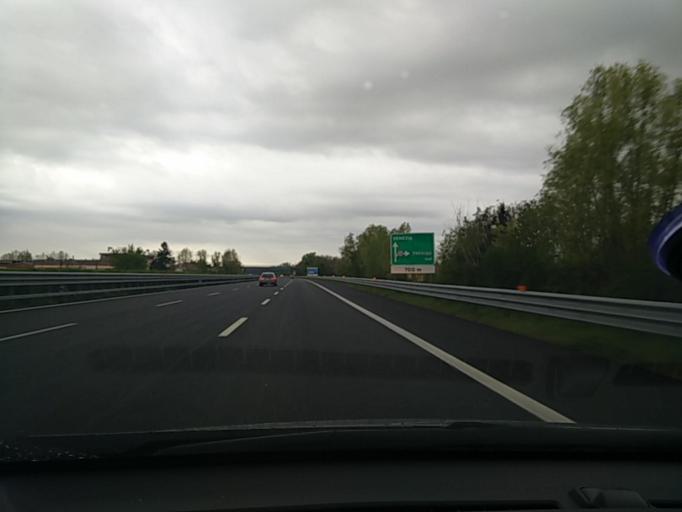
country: IT
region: Veneto
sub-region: Provincia di Treviso
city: Cendon
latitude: 45.6536
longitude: 12.3167
